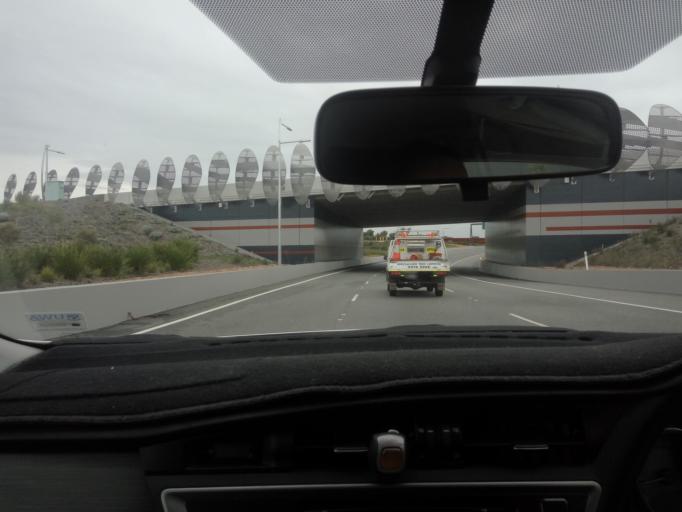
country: AU
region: Western Australia
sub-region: Belmont
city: Kewdale
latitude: -31.9628
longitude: 115.9555
